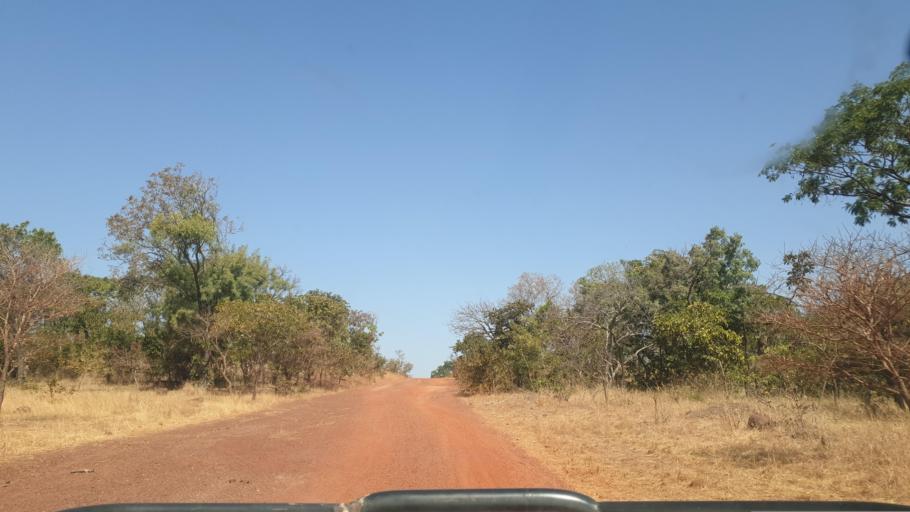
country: ML
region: Koulikoro
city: Dioila
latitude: 11.9120
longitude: -6.9847
